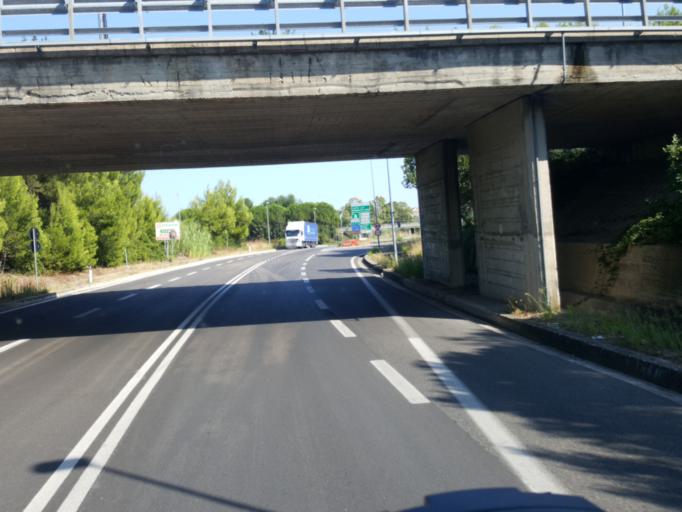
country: IT
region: Abruzzo
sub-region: Provincia di Chieti
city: Salvo Marina
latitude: 42.0604
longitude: 14.7676
